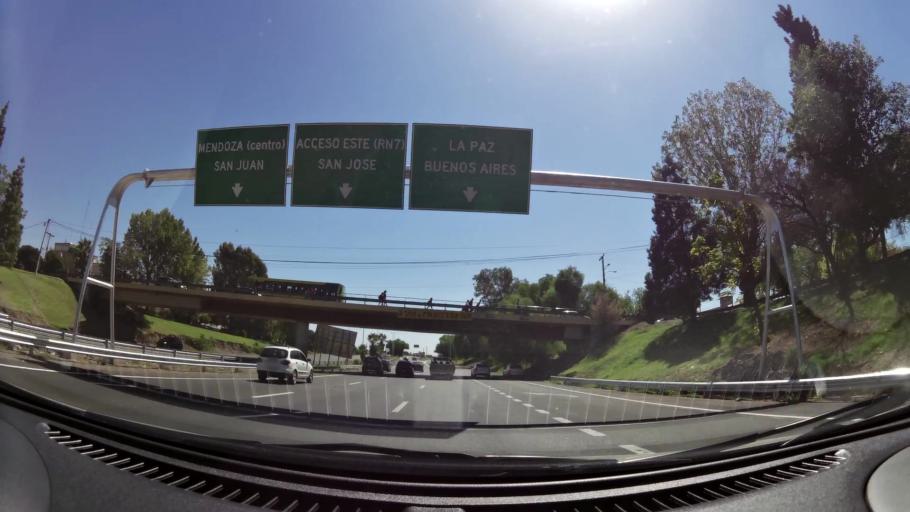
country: AR
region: Mendoza
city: Mendoza
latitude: -32.9006
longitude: -68.8192
